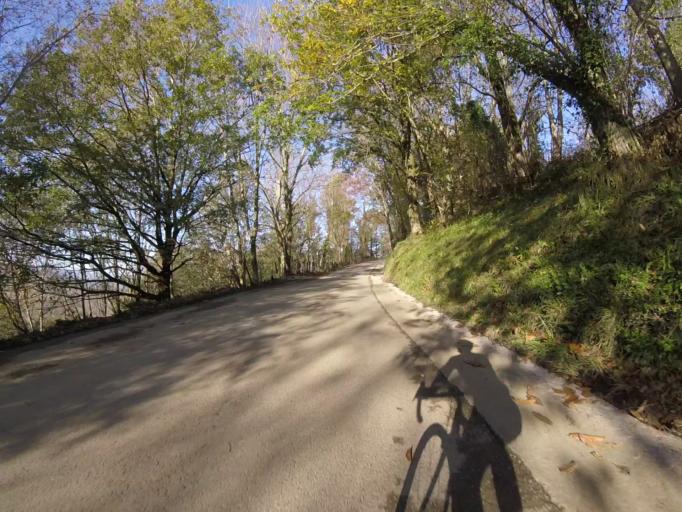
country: ES
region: Basque Country
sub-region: Provincia de Guipuzcoa
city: Usurbil
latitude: 43.2781
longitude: -2.0694
